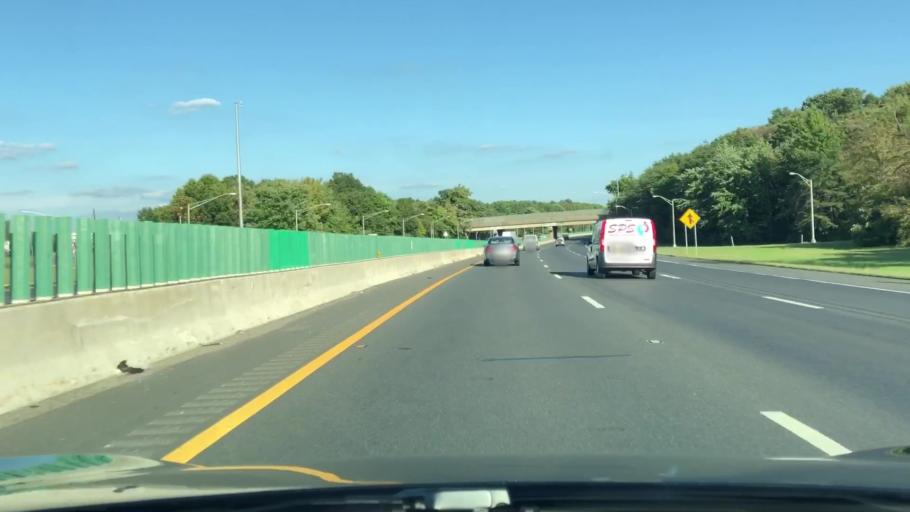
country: US
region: New Jersey
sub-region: Gloucester County
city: Westville
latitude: 39.8610
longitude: -75.1505
